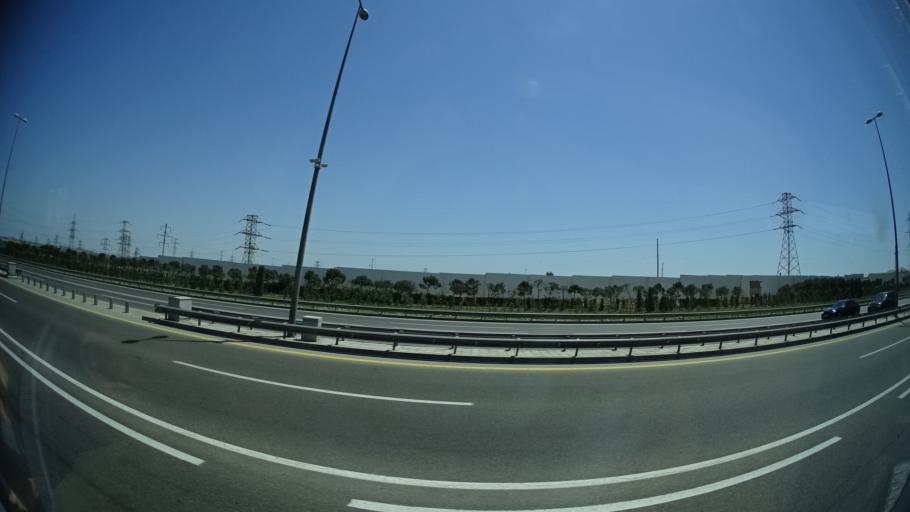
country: AZ
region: Baki
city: Yeni Suraxani
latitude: 40.4381
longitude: 50.0354
